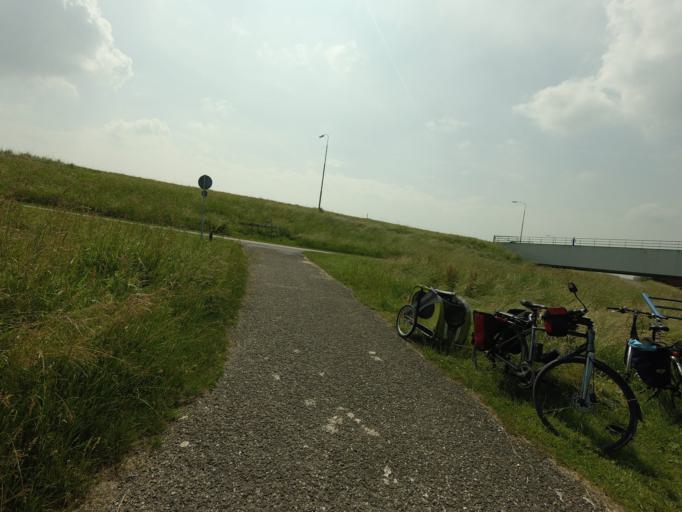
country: NL
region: South Holland
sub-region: Gemeente Gouda
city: Bloemendaal
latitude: 51.9777
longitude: 4.6529
